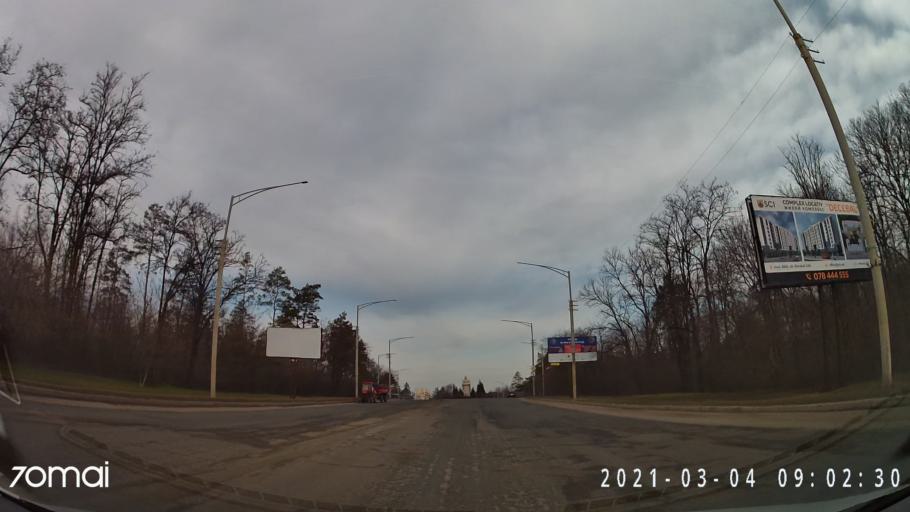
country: MD
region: Balti
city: Balti
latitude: 47.7436
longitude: 27.9542
